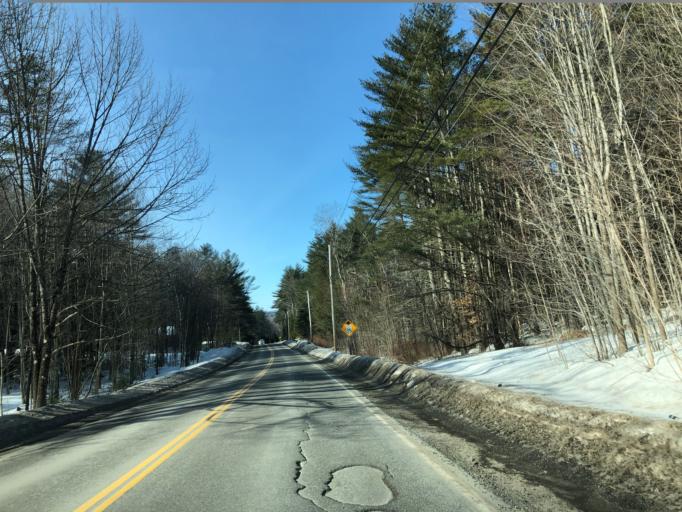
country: US
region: Maine
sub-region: Androscoggin County
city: Mechanic Falls
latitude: 44.1616
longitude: -70.3586
